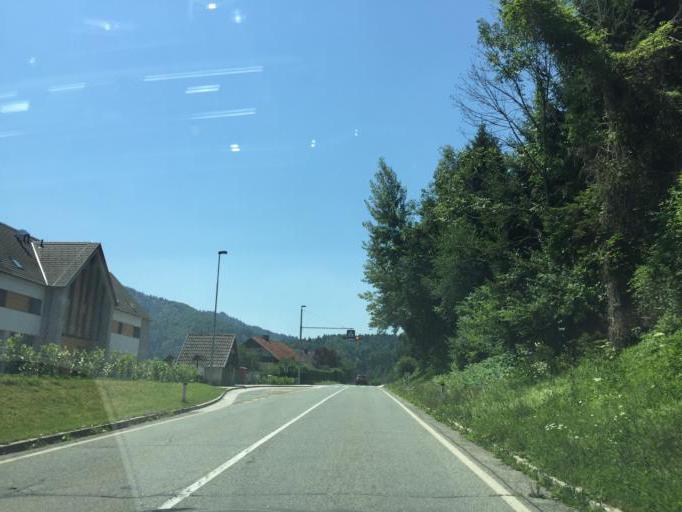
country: SI
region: Skofja Loka
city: Skofja Loka
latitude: 46.1485
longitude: 14.2825
